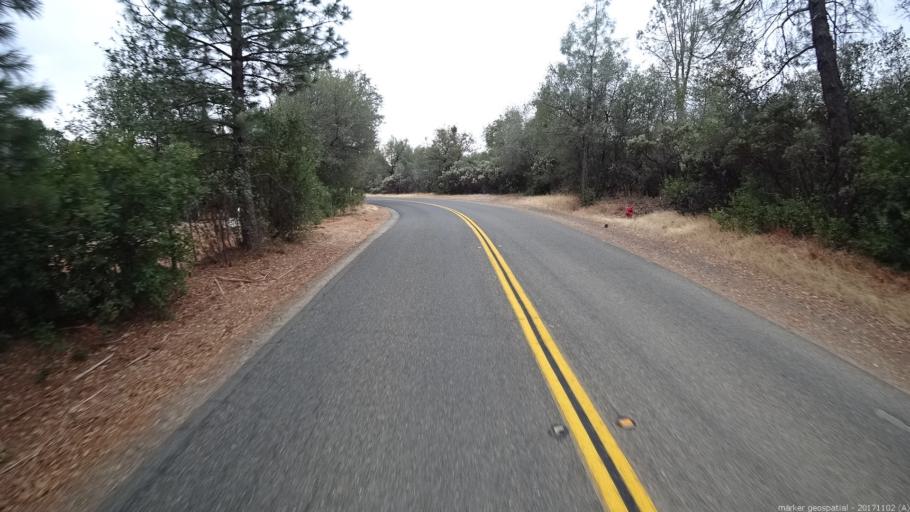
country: US
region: California
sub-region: Shasta County
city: Redding
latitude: 40.6341
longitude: -122.4189
